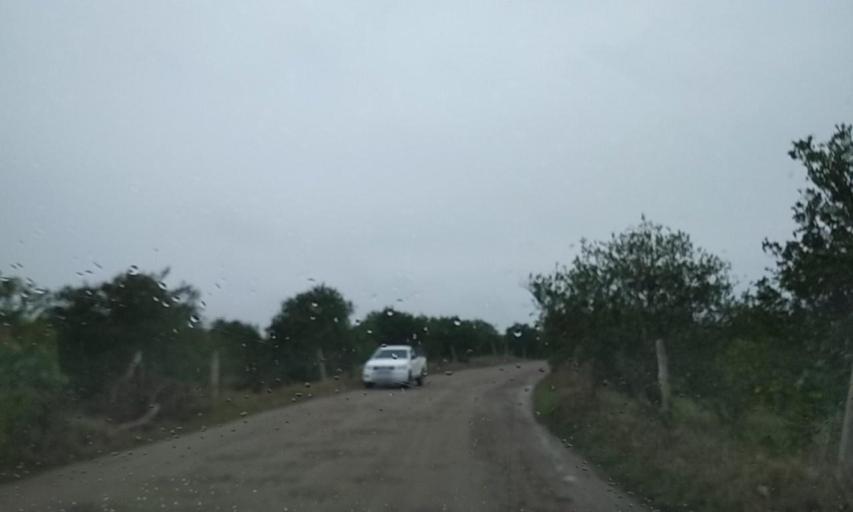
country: MX
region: Veracruz
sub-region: Papantla
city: El Chote
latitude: 20.3372
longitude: -97.3902
